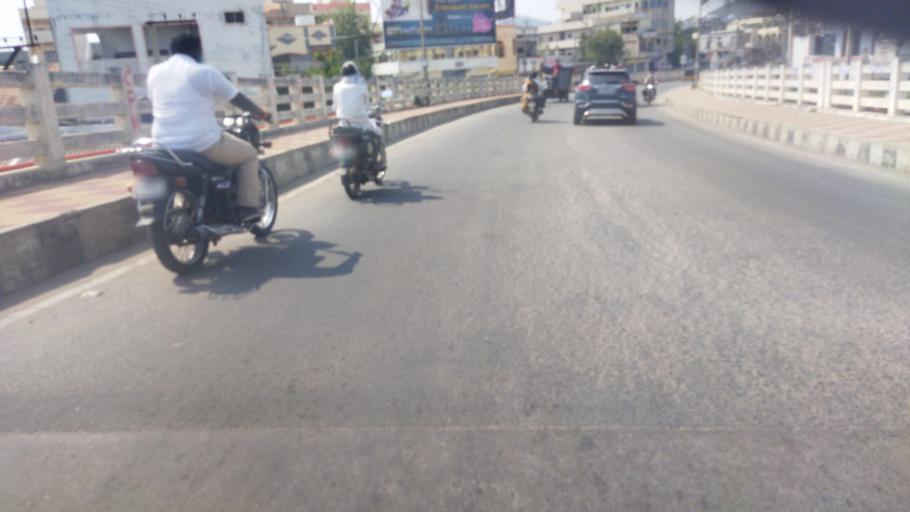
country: IN
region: Telangana
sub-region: Nalgonda
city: Nalgonda
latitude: 17.0643
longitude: 79.2792
